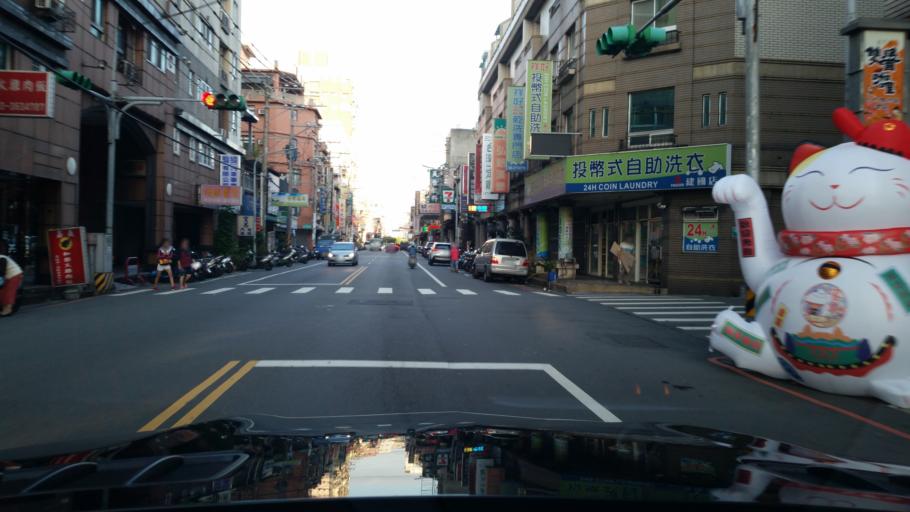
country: TW
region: Taiwan
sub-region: Taoyuan
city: Taoyuan
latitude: 24.9858
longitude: 121.3161
